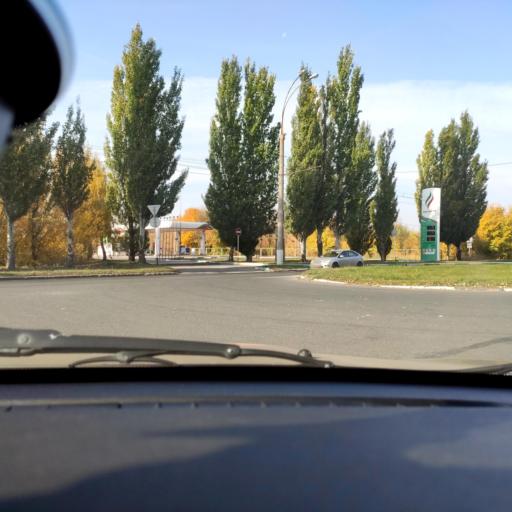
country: RU
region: Samara
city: Tol'yatti
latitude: 53.5497
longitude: 49.2715
